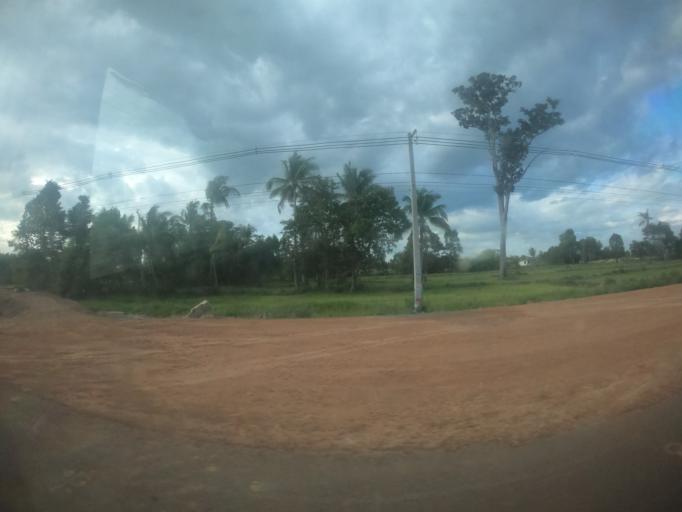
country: TH
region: Surin
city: Kap Choeng
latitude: 14.4573
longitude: 103.6732
